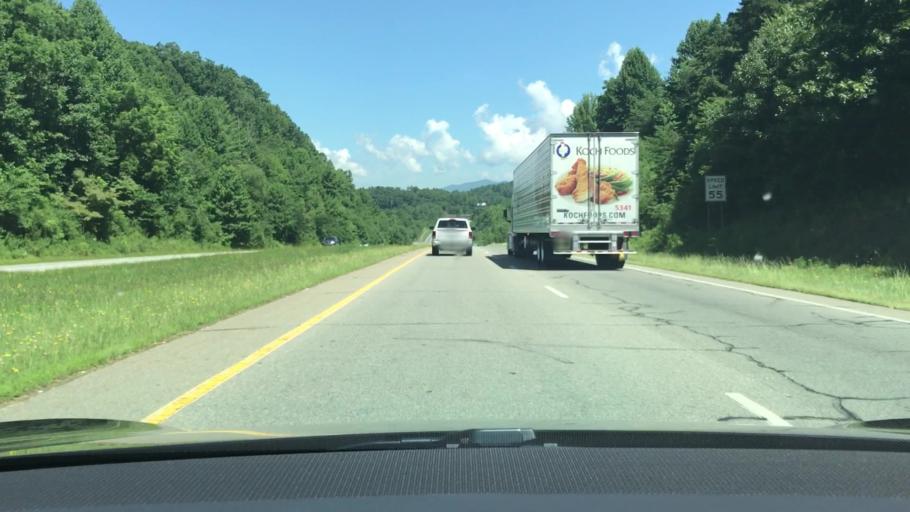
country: US
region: North Carolina
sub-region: Macon County
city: Franklin
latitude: 35.1847
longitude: -83.3579
